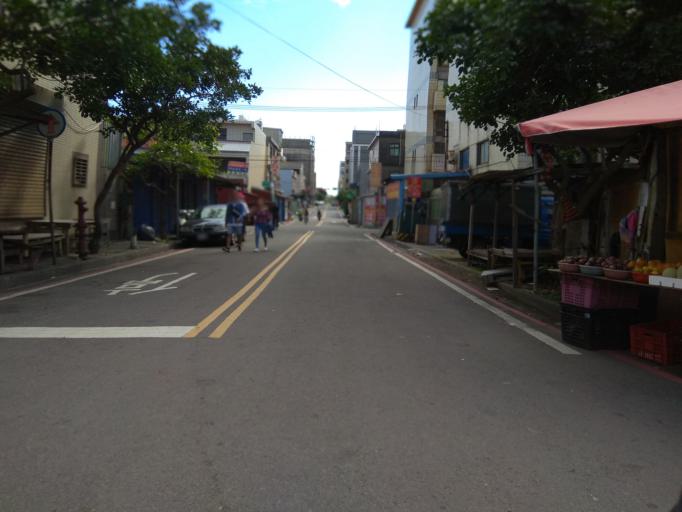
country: TW
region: Taiwan
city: Taoyuan City
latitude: 25.0511
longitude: 121.1187
